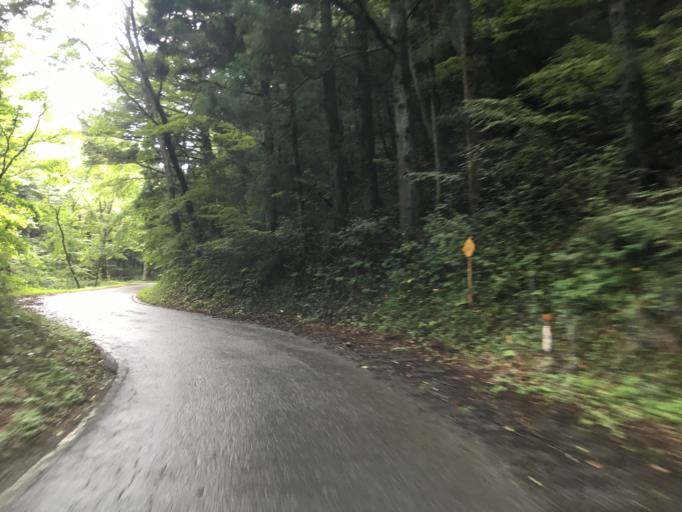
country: JP
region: Miyagi
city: Marumori
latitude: 37.8851
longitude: 140.8607
